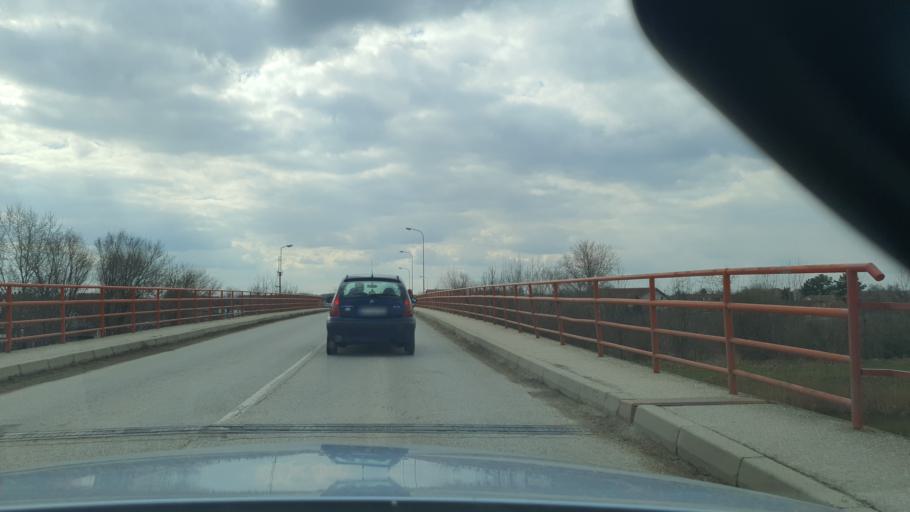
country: RS
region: Autonomna Pokrajina Vojvodina
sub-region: Juznobacki Okrug
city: Bac
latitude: 45.3880
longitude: 19.2326
